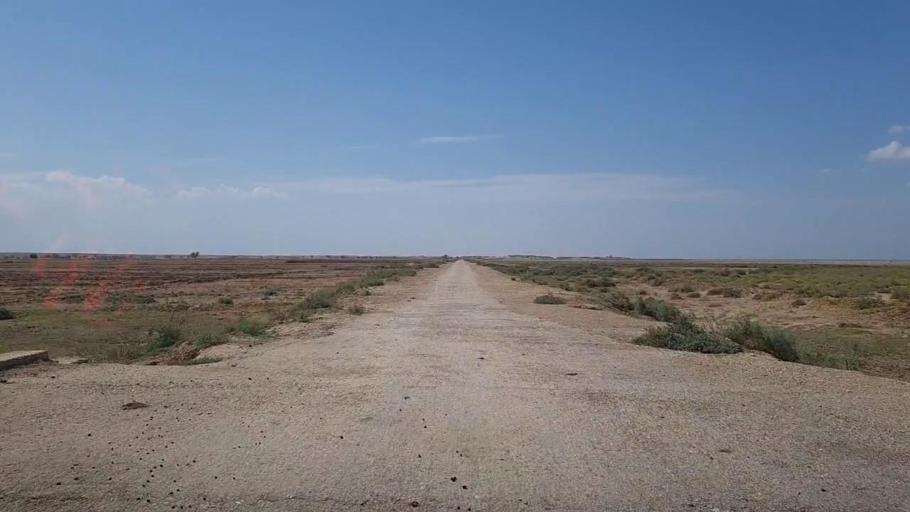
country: PK
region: Sindh
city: Bhan
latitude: 26.3610
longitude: 67.6682
